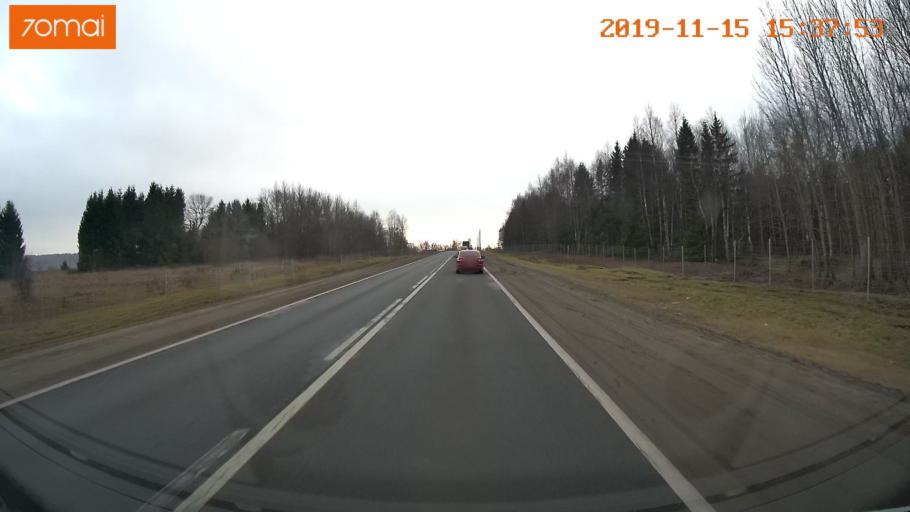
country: RU
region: Jaroslavl
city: Danilov
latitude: 58.0350
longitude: 40.0855
